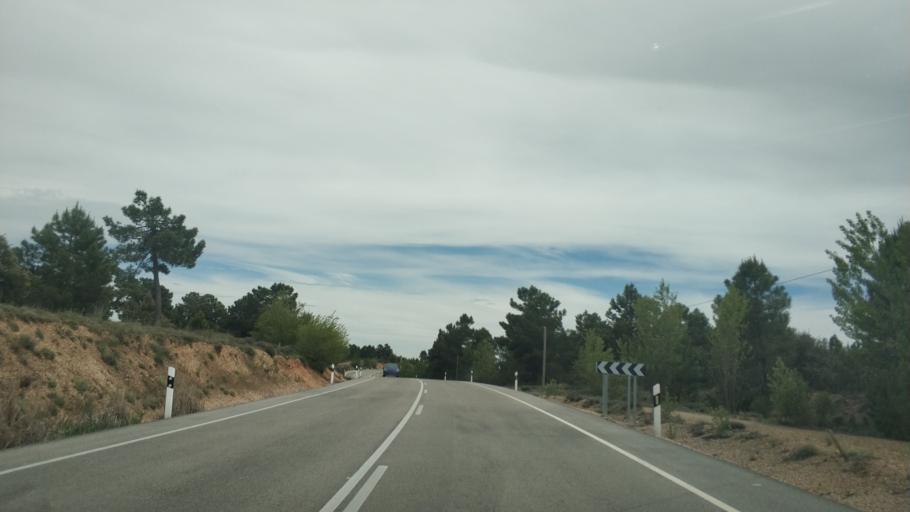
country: ES
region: Castille and Leon
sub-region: Provincia de Soria
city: Quintanas de Gormaz
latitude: 41.5314
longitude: -2.9485
